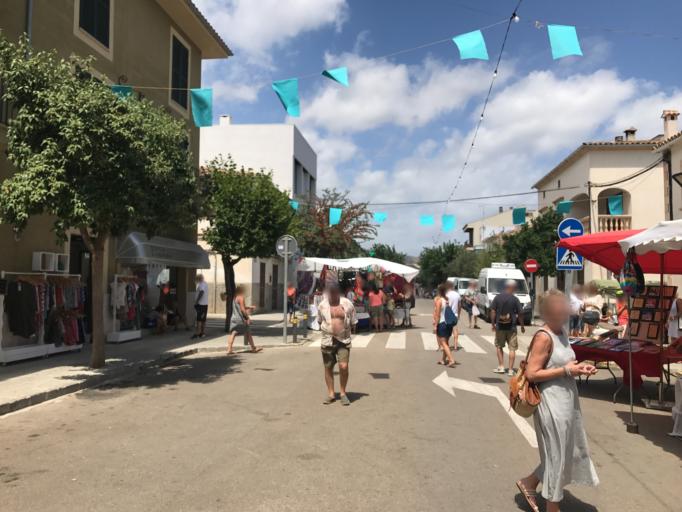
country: ES
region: Balearic Islands
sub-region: Illes Balears
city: Arta
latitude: 39.6925
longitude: 3.3483
